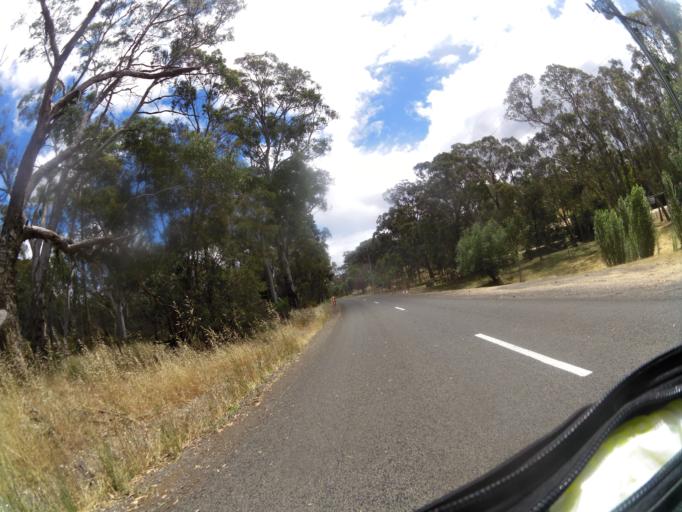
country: AU
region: Victoria
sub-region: Mount Alexander
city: Castlemaine
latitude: -37.0306
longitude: 144.2462
